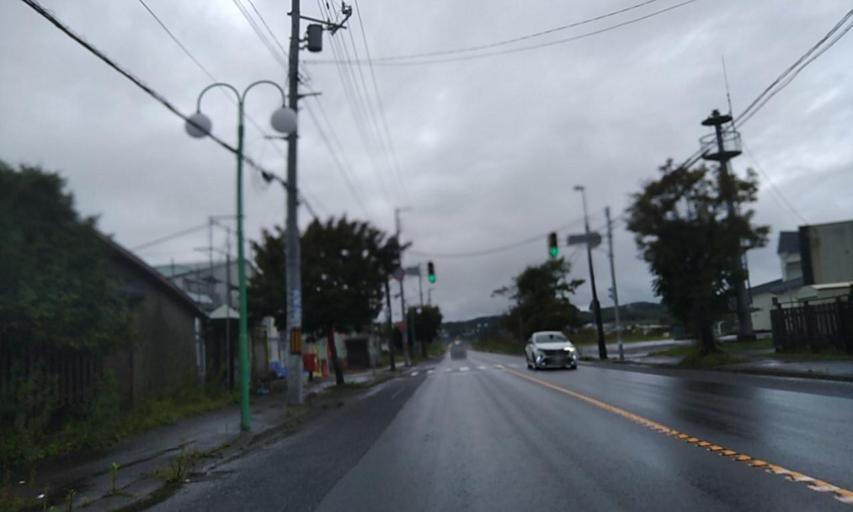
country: JP
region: Hokkaido
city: Kushiro
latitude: 42.9822
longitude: 144.1459
